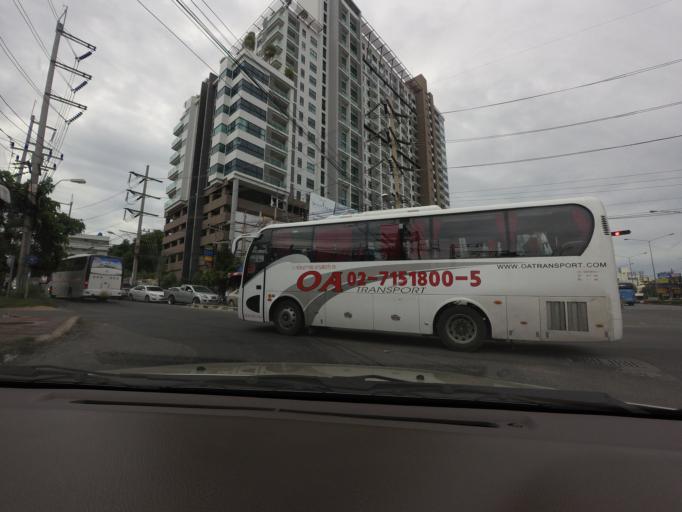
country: TH
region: Chon Buri
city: Phatthaya
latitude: 12.9115
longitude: 100.8692
